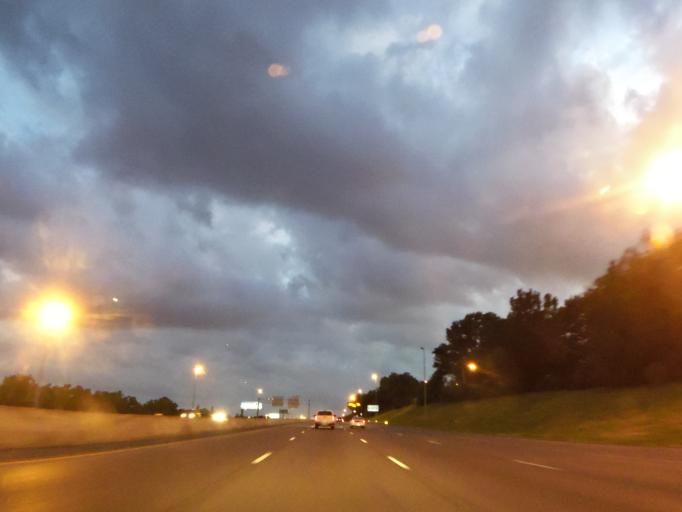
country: US
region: Illinois
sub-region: Saint Clair County
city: Cahokia
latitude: 38.5857
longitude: -90.2172
